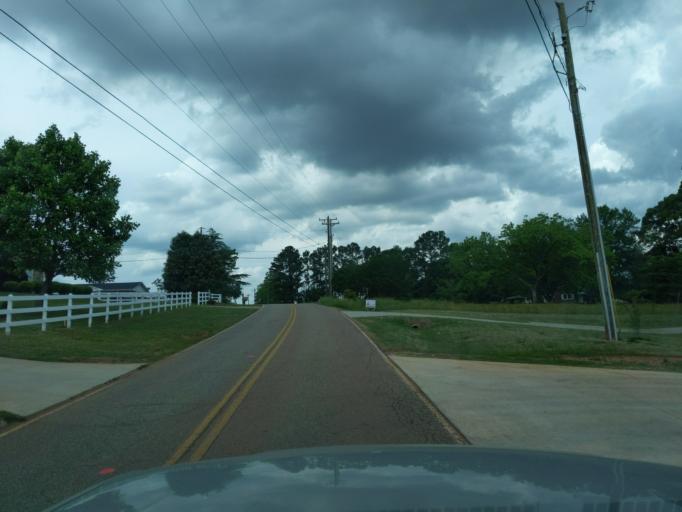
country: US
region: South Carolina
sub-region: Spartanburg County
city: Inman Mills
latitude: 35.0265
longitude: -82.1254
